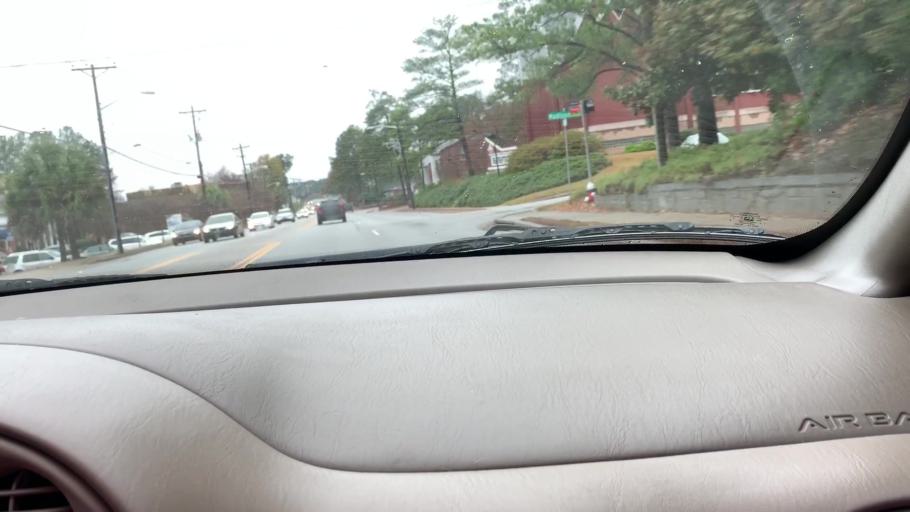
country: US
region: South Carolina
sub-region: Richland County
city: Forest Acres
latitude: 34.0205
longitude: -80.9833
